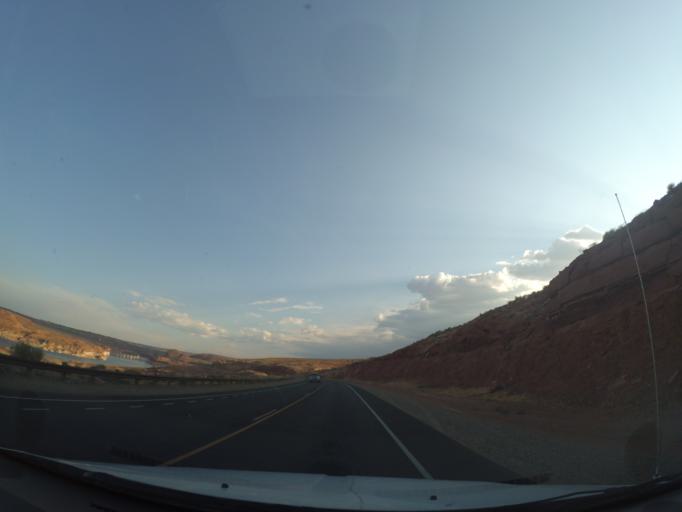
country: US
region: Arizona
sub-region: Coconino County
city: Page
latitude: 36.9611
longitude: -111.4933
